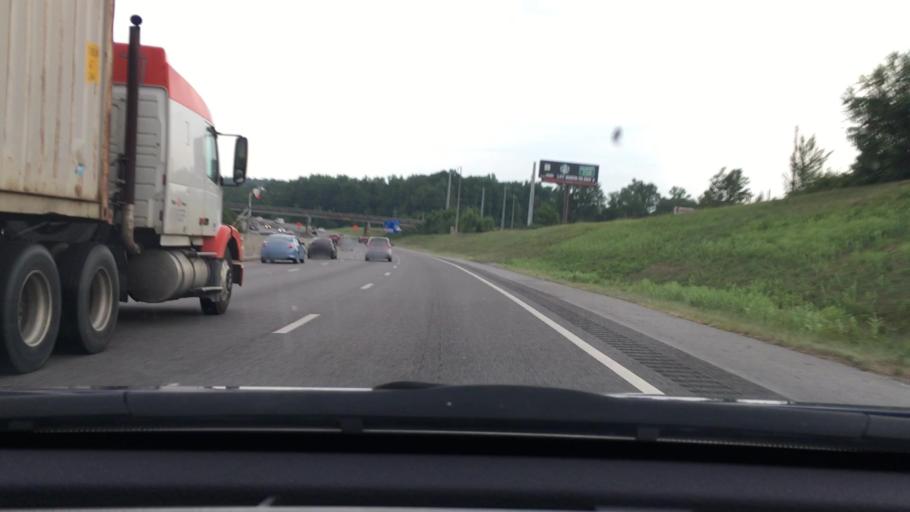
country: US
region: South Carolina
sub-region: Lexington County
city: Springdale
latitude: 33.9407
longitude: -81.0881
